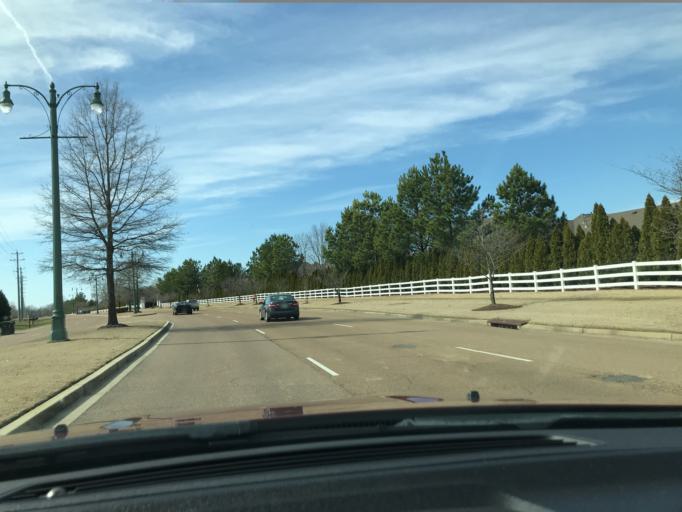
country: US
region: Tennessee
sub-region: Shelby County
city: Collierville
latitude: 35.0408
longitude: -89.7116
